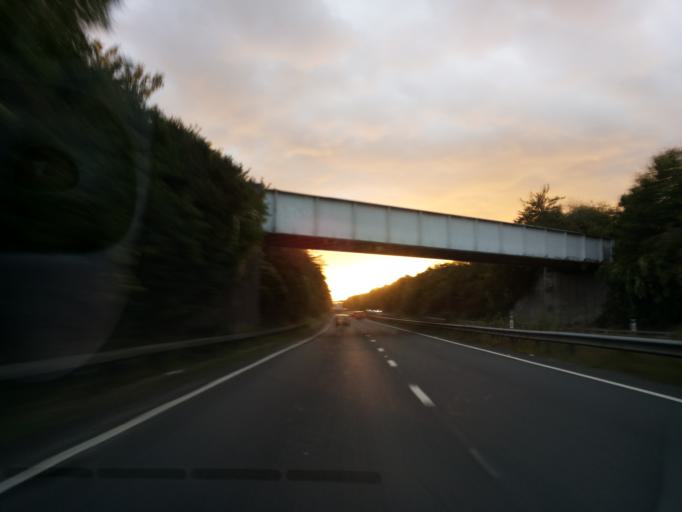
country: GB
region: England
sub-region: Hampshire
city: Abbotts Ann
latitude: 51.2133
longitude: -1.5589
